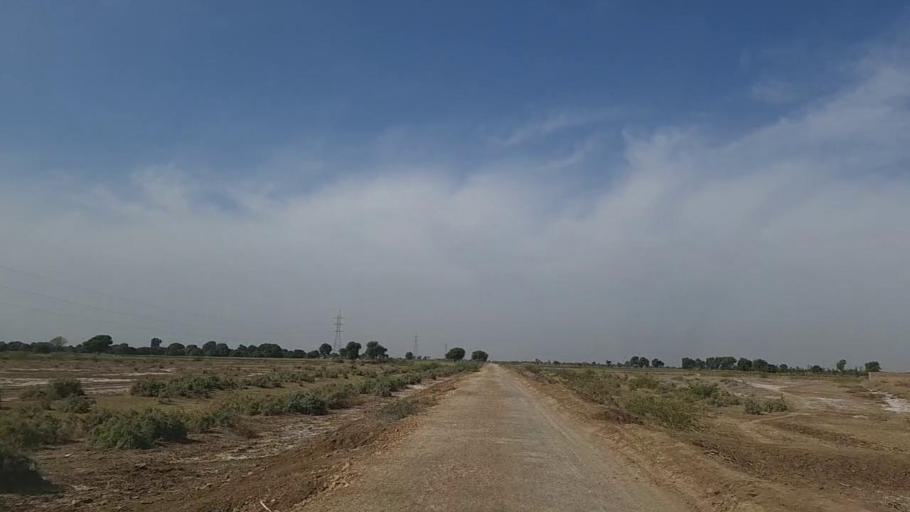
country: PK
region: Sindh
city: Samaro
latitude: 25.2135
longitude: 69.4541
